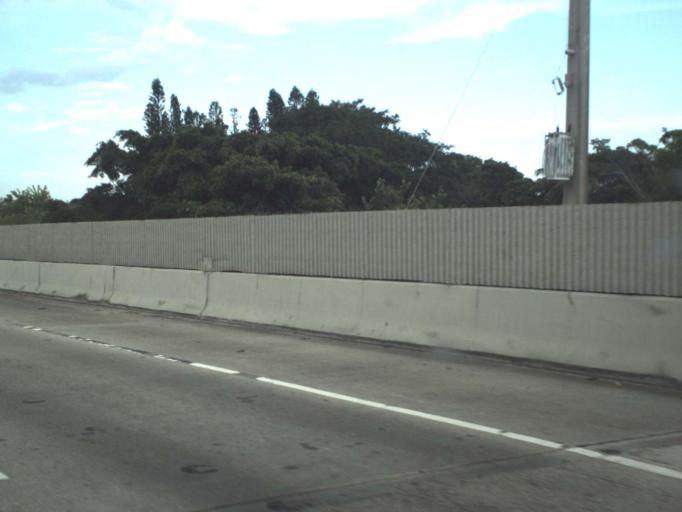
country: US
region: Florida
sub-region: Palm Beach County
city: Lake Clarke Shores
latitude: 26.6657
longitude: -80.0707
